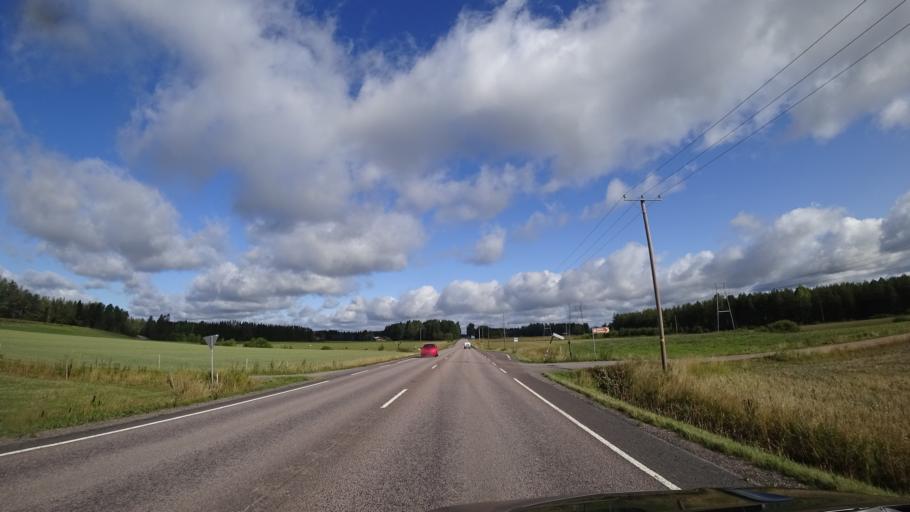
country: FI
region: Uusimaa
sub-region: Helsinki
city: Hyvinge
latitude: 60.5193
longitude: 24.9259
